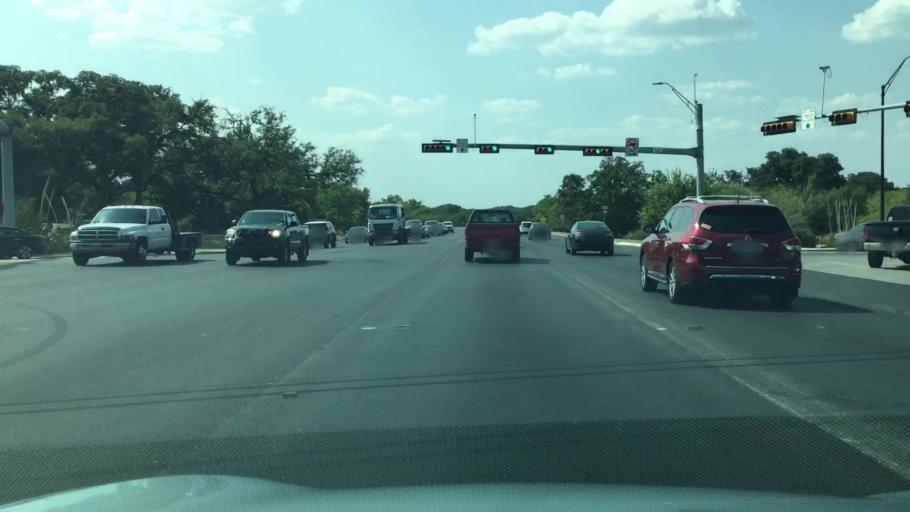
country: US
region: Texas
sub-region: Hays County
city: San Marcos
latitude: 29.8655
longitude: -97.9631
